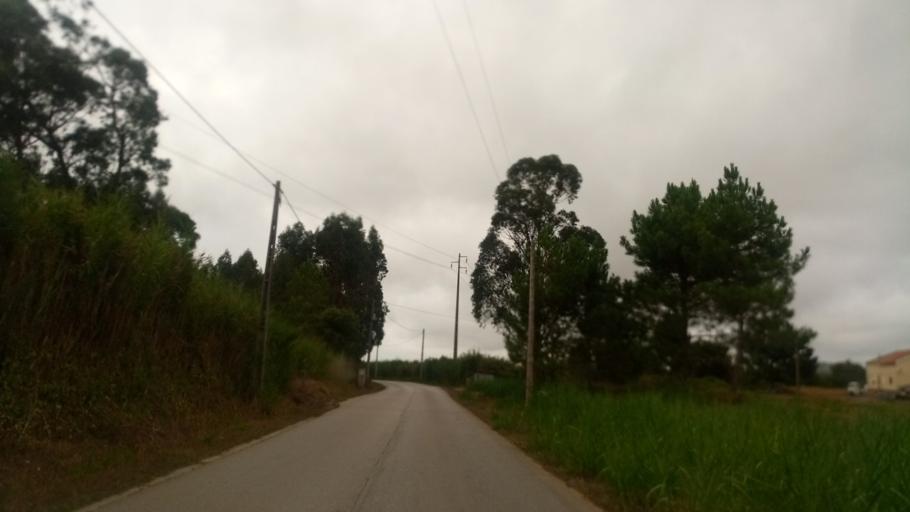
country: PT
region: Leiria
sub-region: Caldas da Rainha
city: Caldas da Rainha
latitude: 39.4208
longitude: -9.1397
